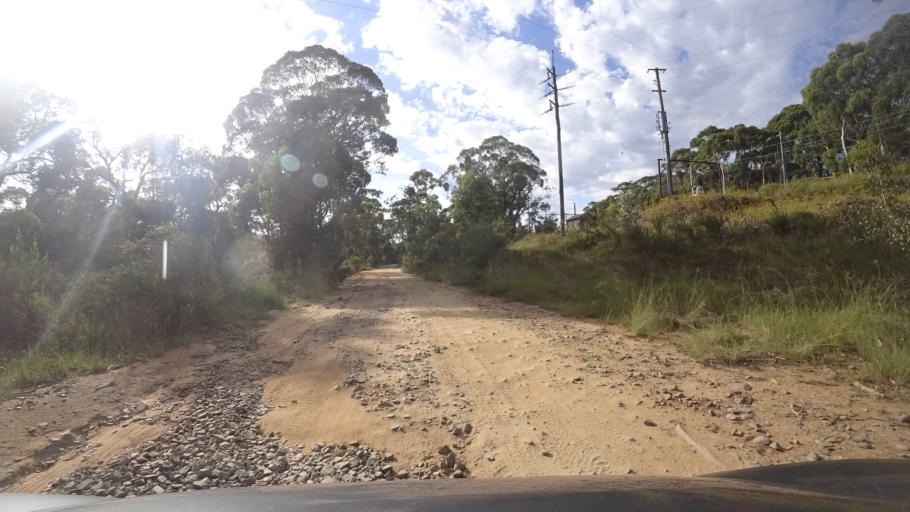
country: AU
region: New South Wales
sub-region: Lithgow
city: Lithgow
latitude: -33.4775
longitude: 150.2453
